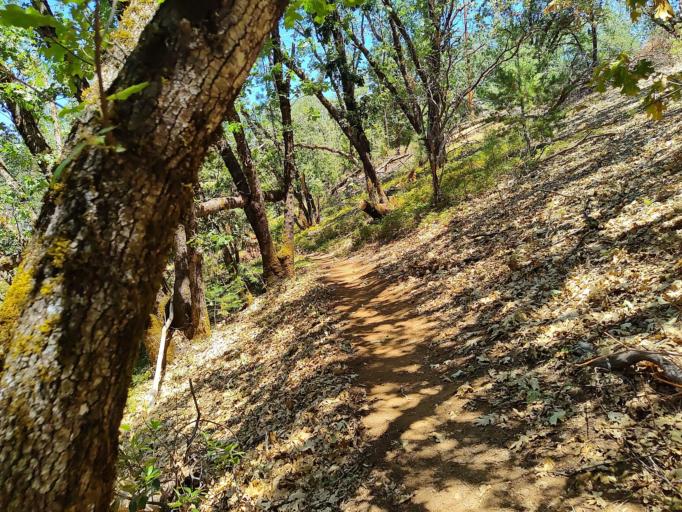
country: US
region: California
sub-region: Placer County
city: Meadow Vista
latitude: 39.0350
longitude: -120.9873
